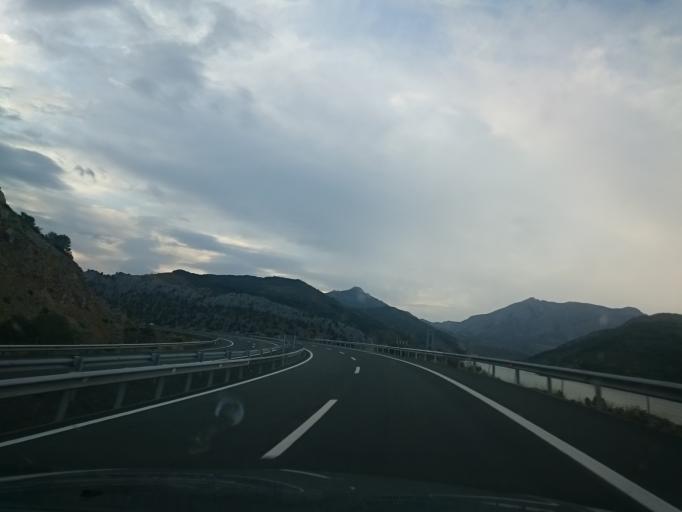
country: ES
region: Castille and Leon
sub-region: Provincia de Leon
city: Sena de Luna
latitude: 42.8782
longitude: -5.8809
